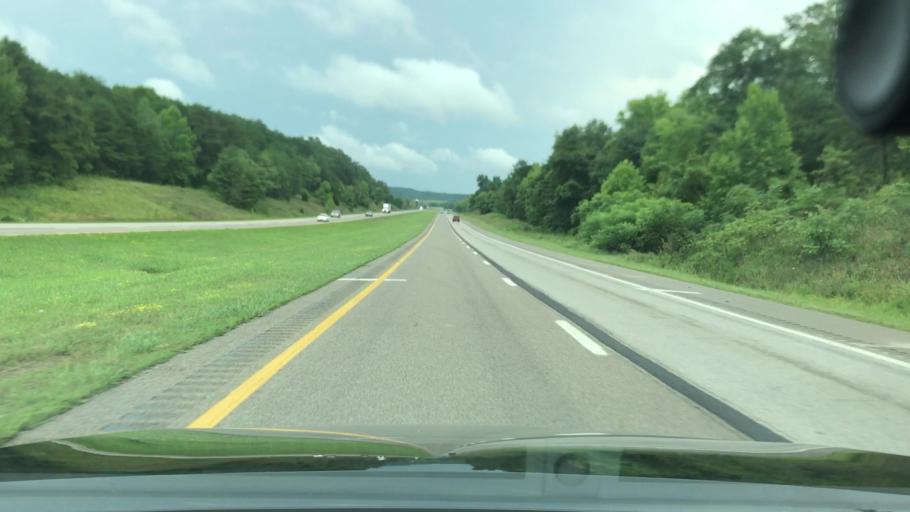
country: US
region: Ohio
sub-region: Gallia County
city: Gallipolis
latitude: 38.8681
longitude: -82.2718
